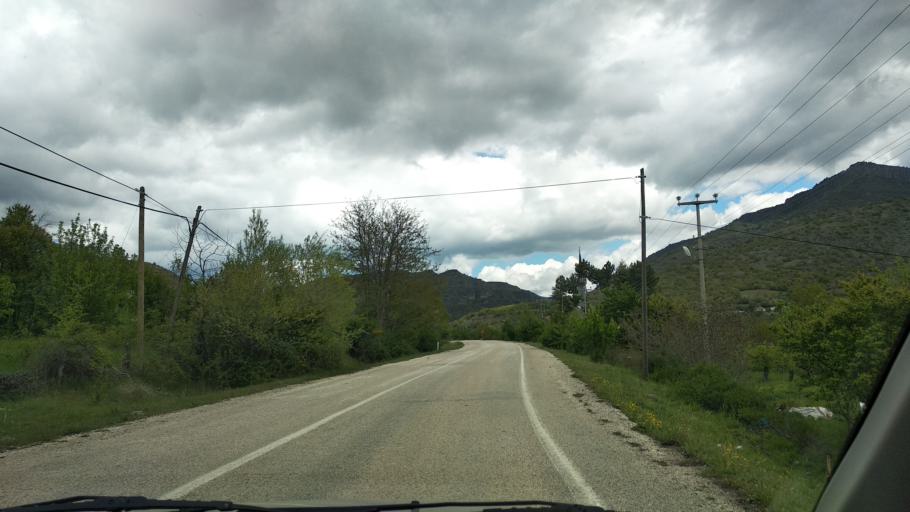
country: TR
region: Bolu
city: Seben
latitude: 40.4186
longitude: 31.5824
